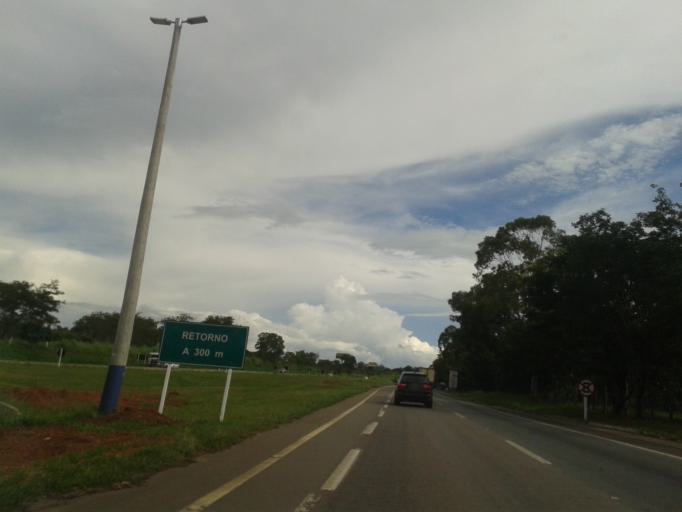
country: BR
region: Goias
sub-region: Hidrolandia
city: Hidrolandia
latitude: -16.9232
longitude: -49.2526
